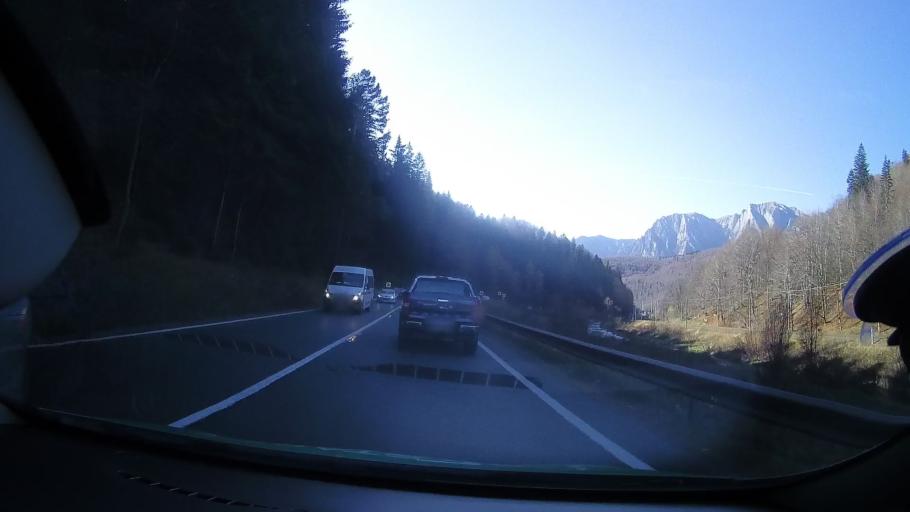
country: RO
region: Prahova
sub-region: Oras Azuga
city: Azuga
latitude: 45.4537
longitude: 25.5647
